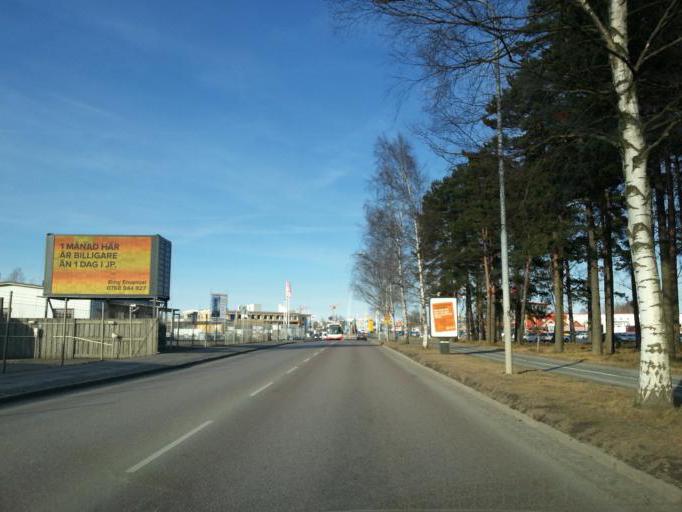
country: SE
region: Joenkoeping
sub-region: Jonkopings Kommun
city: Jonkoping
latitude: 57.7702
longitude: 14.1734
